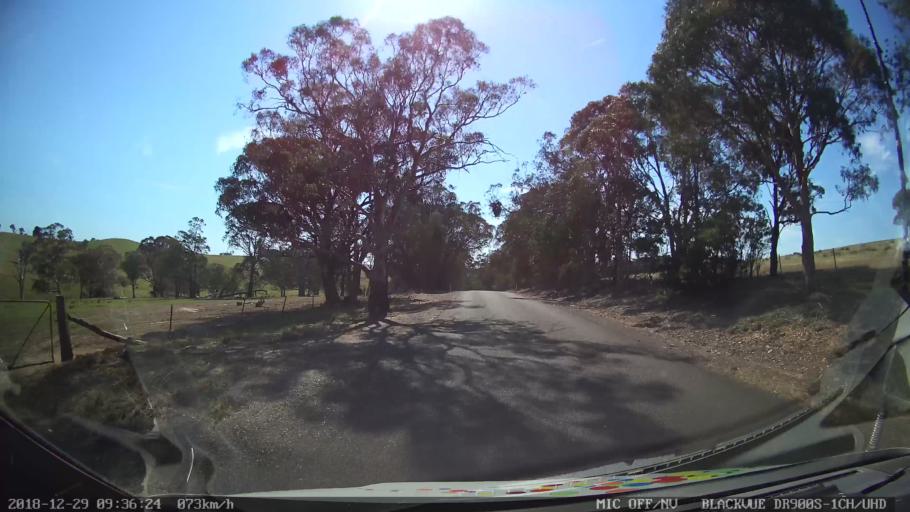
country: AU
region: New South Wales
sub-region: Upper Lachlan Shire
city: Crookwell
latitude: -34.6335
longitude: 149.3636
